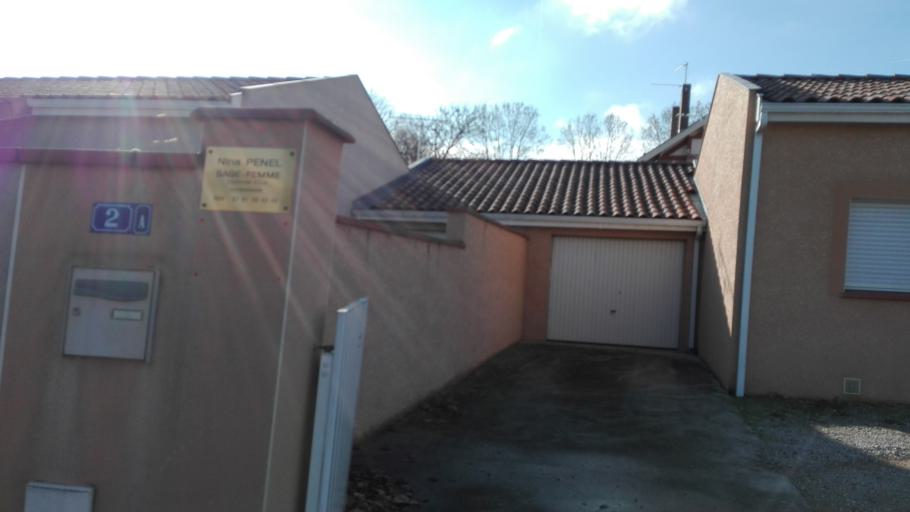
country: FR
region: Midi-Pyrenees
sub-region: Departement de la Haute-Garonne
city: Grenade
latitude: 43.7674
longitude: 1.2980
